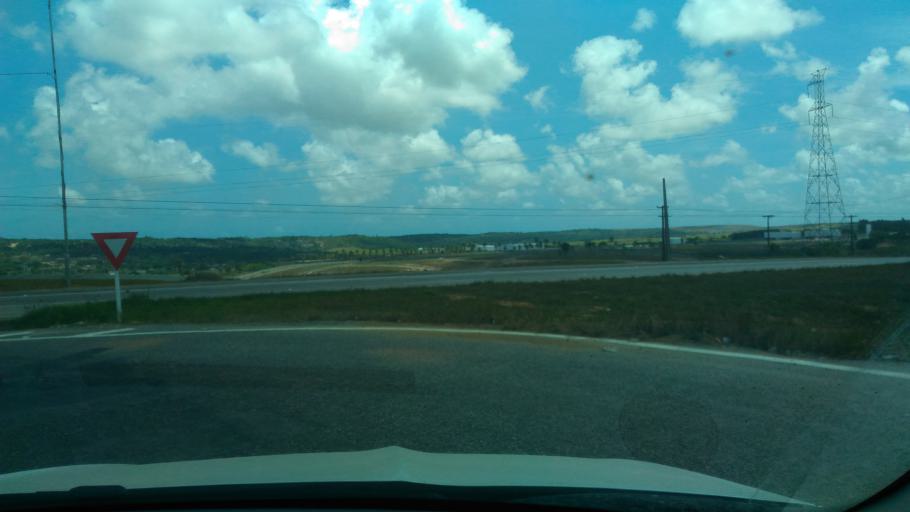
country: BR
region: Paraiba
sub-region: Conde
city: Conde
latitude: -7.2612
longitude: -34.9361
